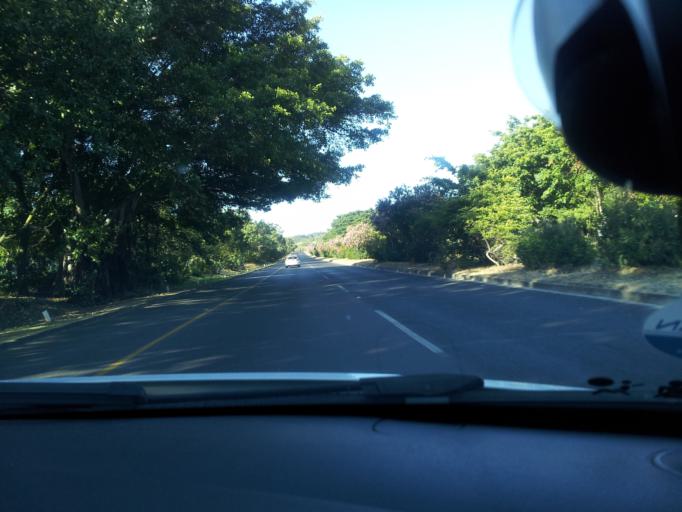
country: ZA
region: Western Cape
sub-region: Cape Winelands District Municipality
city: Stellenbosch
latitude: -34.0673
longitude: 18.8263
